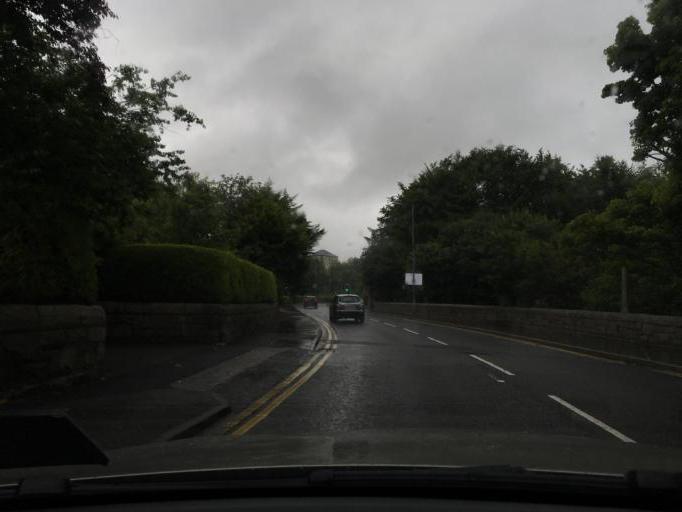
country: GB
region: Northern Ireland
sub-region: Fermanagh District
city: Enniskillen
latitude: 54.3485
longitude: -7.6397
